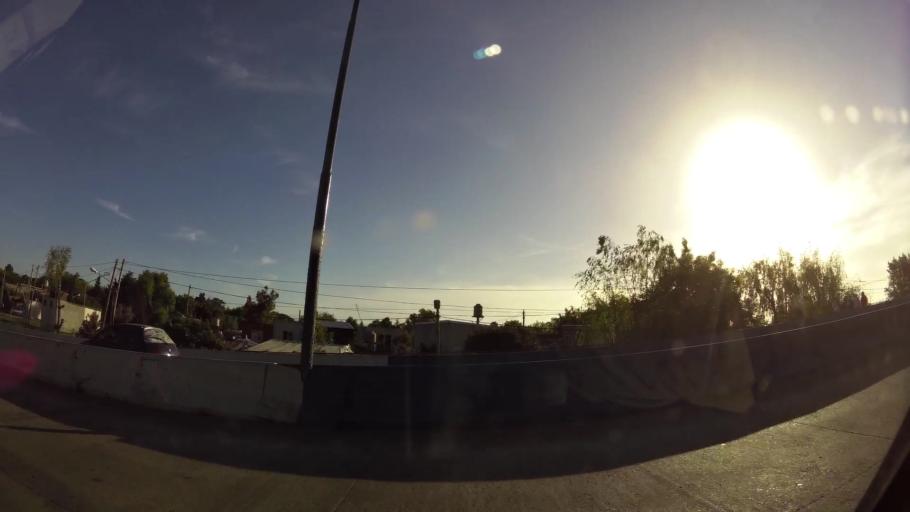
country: AR
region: Buenos Aires
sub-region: Partido de Quilmes
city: Quilmes
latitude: -34.8015
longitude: -58.2084
